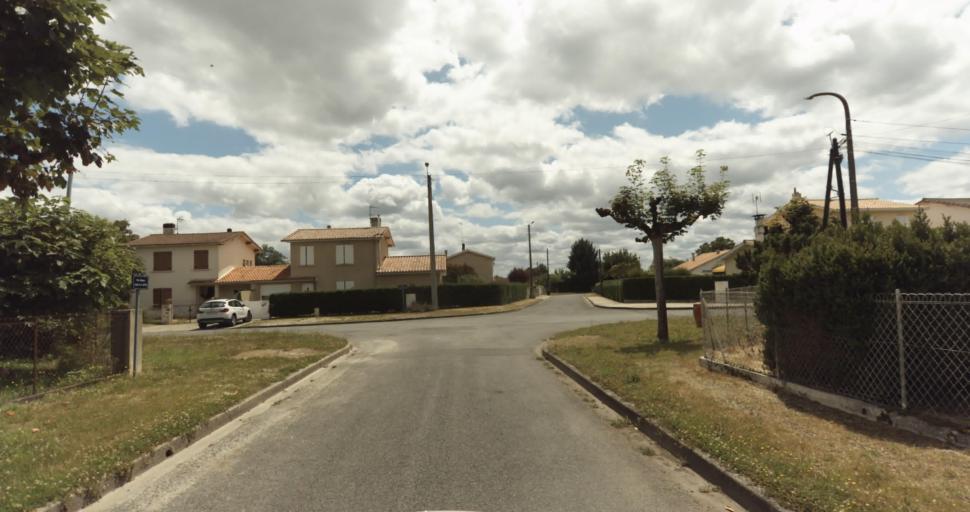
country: FR
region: Aquitaine
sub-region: Departement de la Gironde
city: Bazas
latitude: 44.4366
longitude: -0.2265
